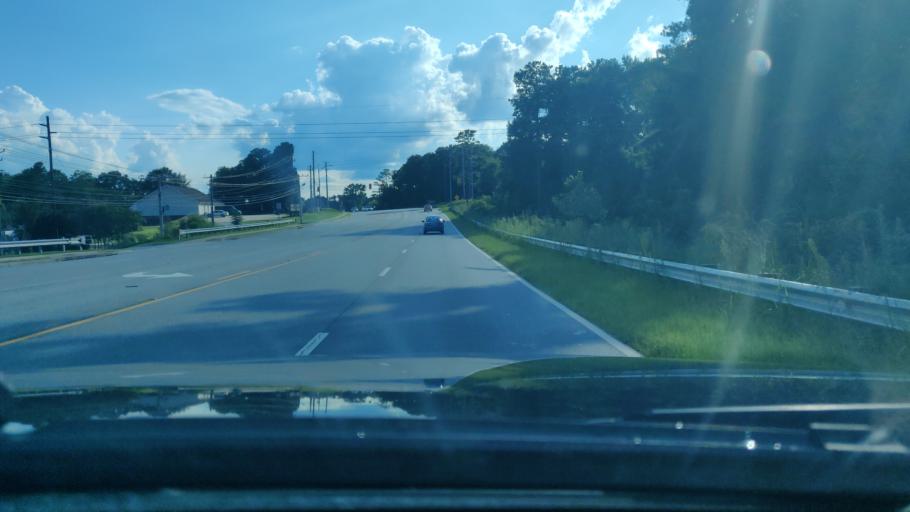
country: US
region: Alabama
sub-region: Lee County
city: Opelika
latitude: 32.6204
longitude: -85.4177
